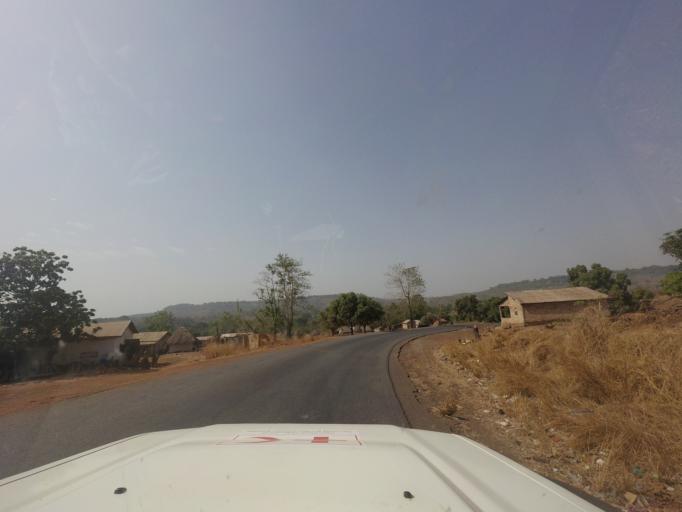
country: GN
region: Mamou
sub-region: Mamou Prefecture
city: Mamou
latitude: 10.1865
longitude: -12.4571
